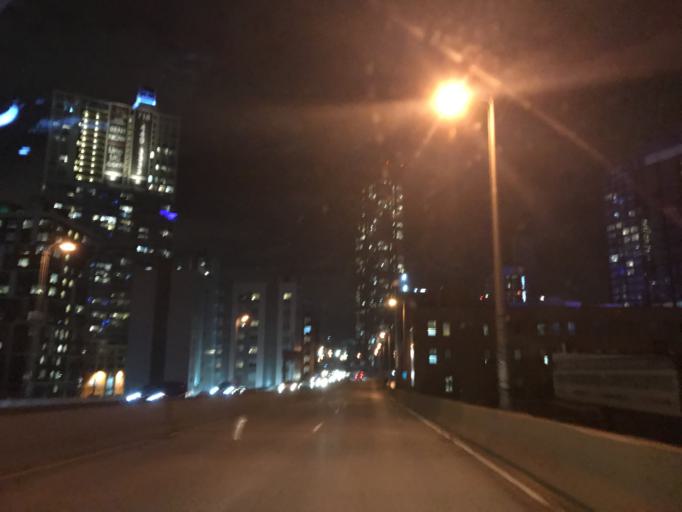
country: US
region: New York
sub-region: Queens County
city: Long Island City
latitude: 40.7470
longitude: -73.9401
